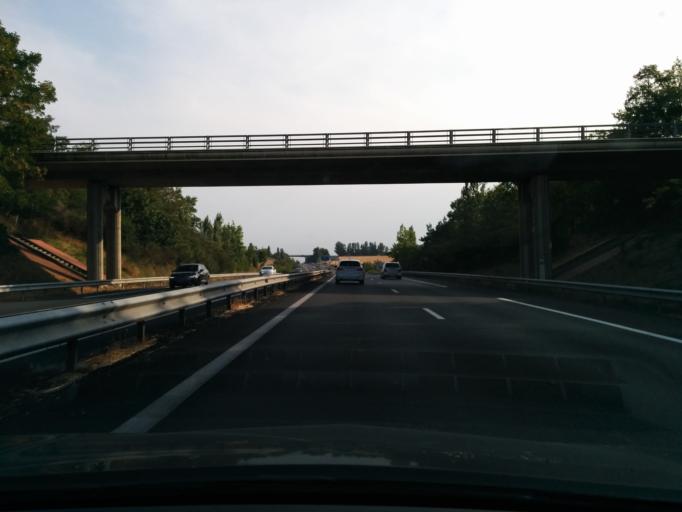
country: FR
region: Midi-Pyrenees
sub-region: Departement de la Haute-Garonne
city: Montastruc-la-Conseillere
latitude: 43.7308
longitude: 1.5761
